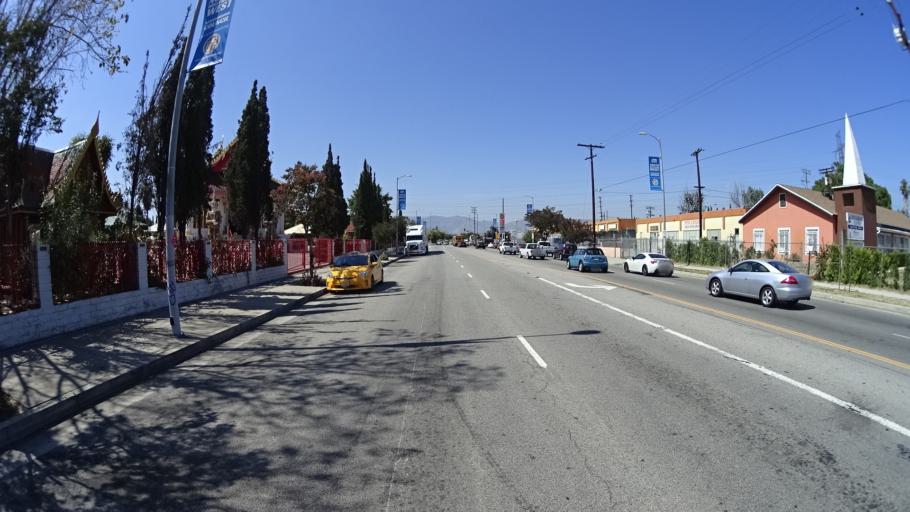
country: US
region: California
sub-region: Los Angeles County
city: Van Nuys
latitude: 34.2202
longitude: -118.4144
